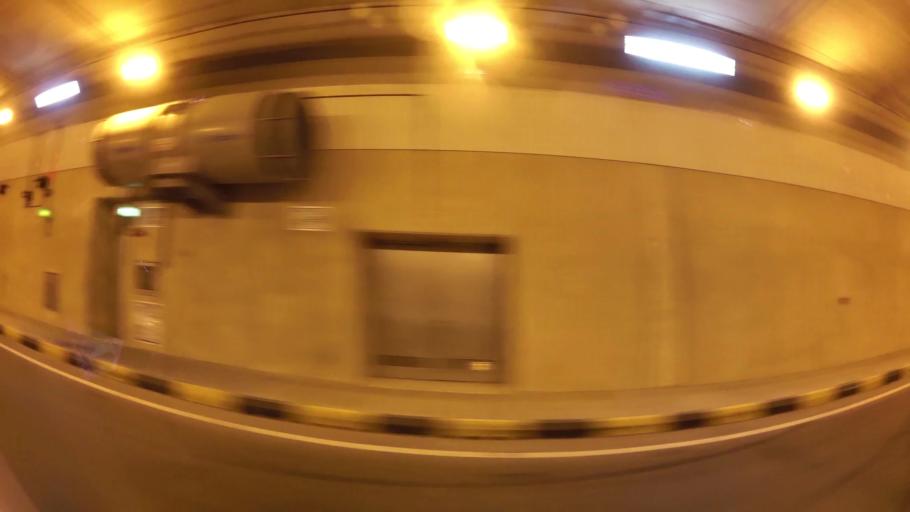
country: AE
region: Abu Dhabi
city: Abu Dhabi
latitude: 24.4614
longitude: 54.6122
